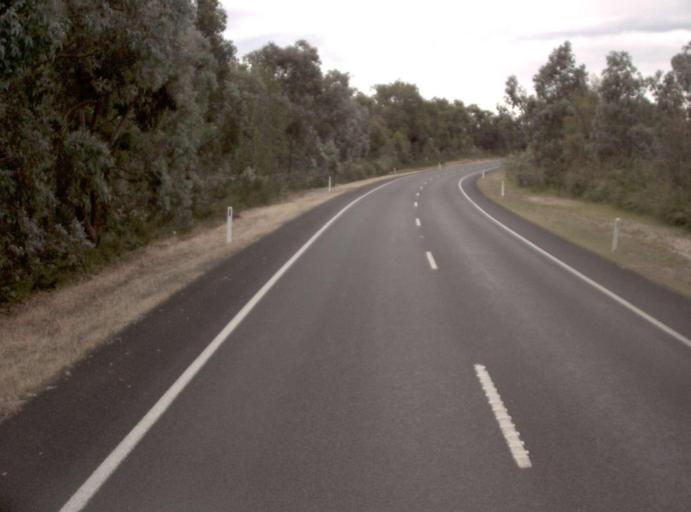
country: AU
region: Victoria
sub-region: Wellington
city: Sale
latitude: -38.3410
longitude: 147.0057
